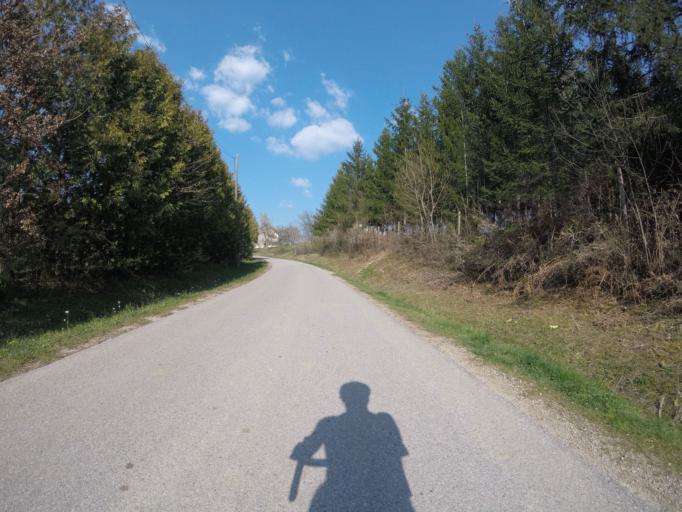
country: HR
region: Sisacko-Moslavacka
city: Gvozd
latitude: 45.4985
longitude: 15.9927
